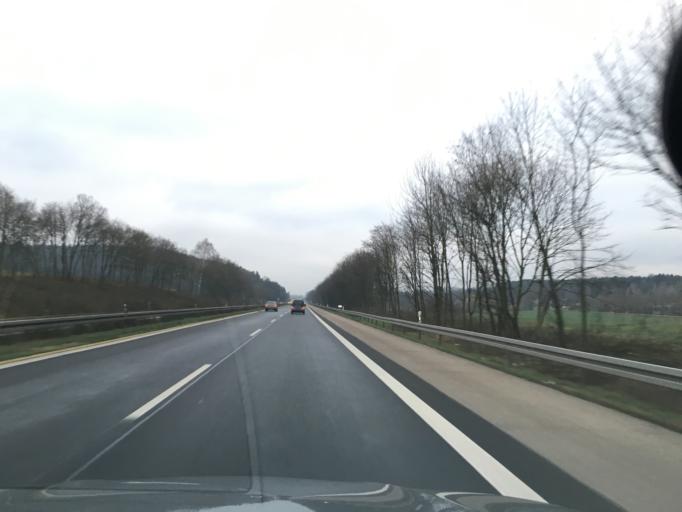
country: DE
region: Bavaria
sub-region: Regierungsbezirk Unterfranken
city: Geiselwind
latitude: 49.7748
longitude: 10.4586
